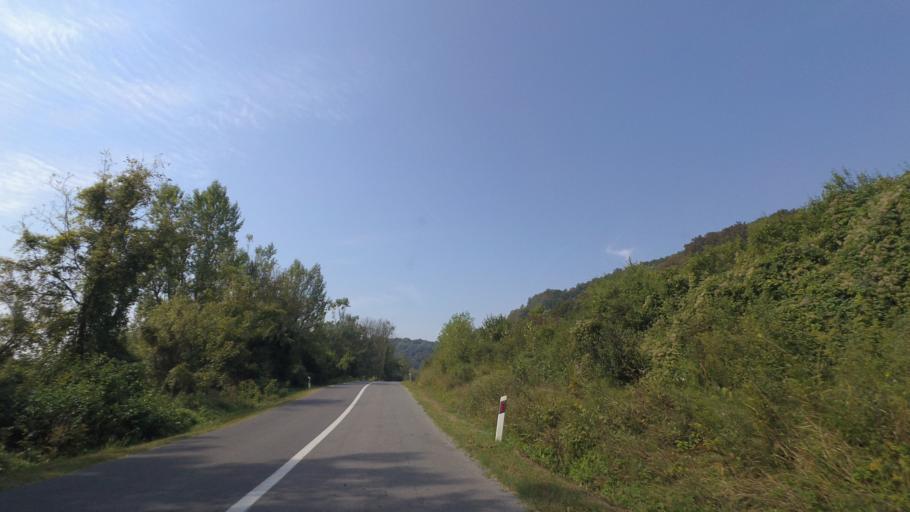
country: HR
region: Sisacko-Moslavacka
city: Dvor
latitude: 45.1162
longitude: 16.3987
